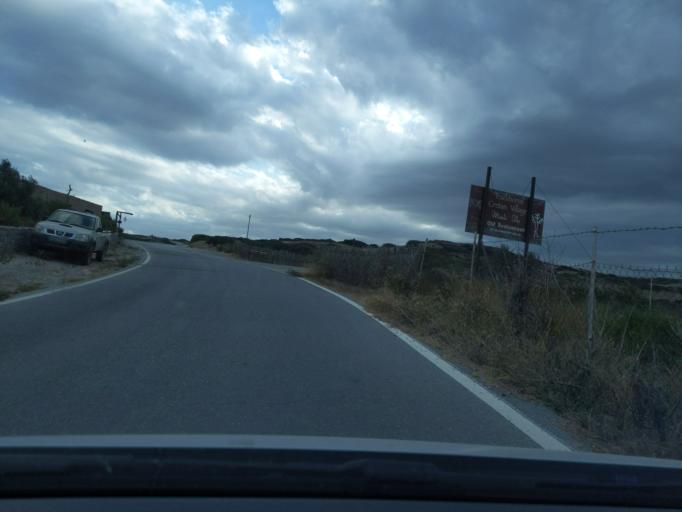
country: GR
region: Crete
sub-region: Nomos Lasithiou
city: Palekastro
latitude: 35.2504
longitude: 26.2512
